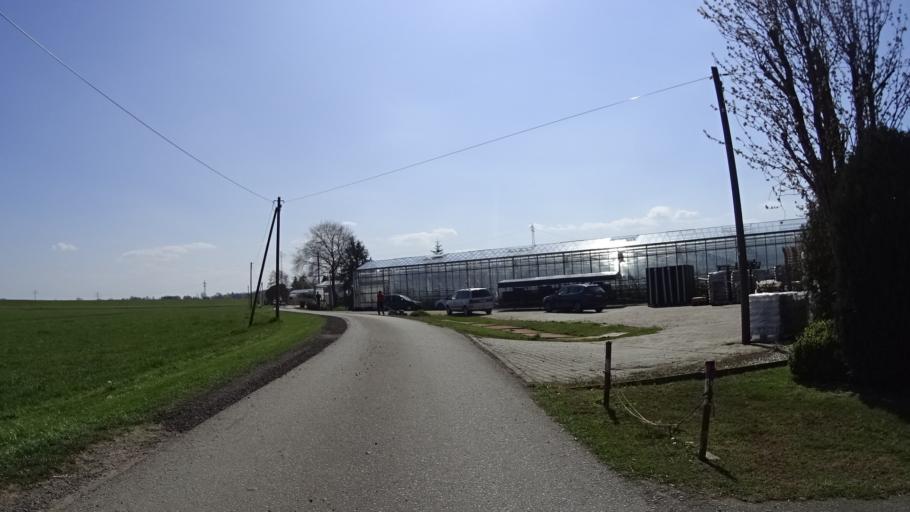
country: DE
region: Lower Saxony
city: Weener
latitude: 53.1116
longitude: 7.3601
